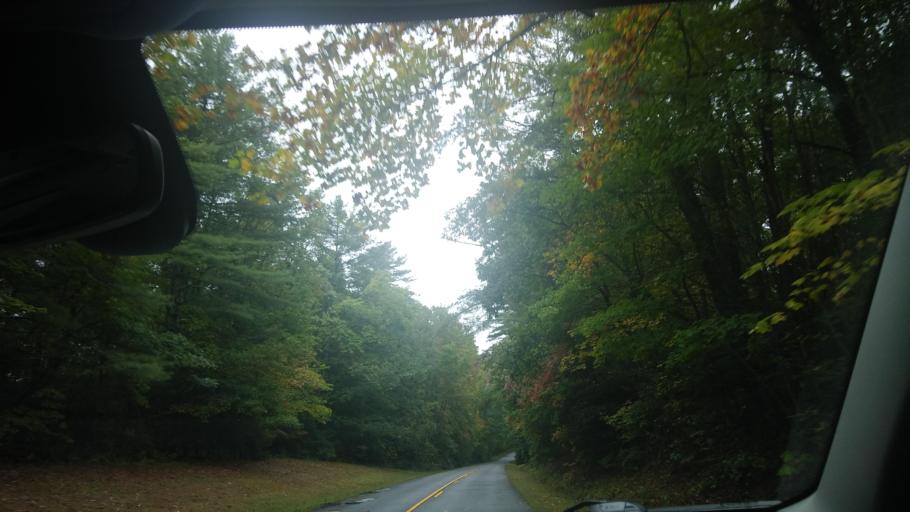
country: US
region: North Carolina
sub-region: Mitchell County
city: Spruce Pine
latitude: 35.8944
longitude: -81.9800
